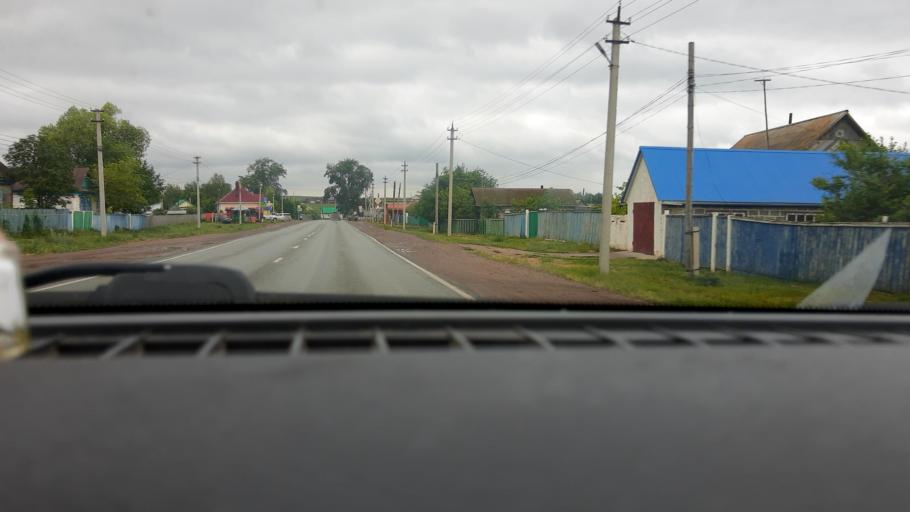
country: RU
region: Bashkortostan
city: Kandry
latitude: 54.3999
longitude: 54.0136
